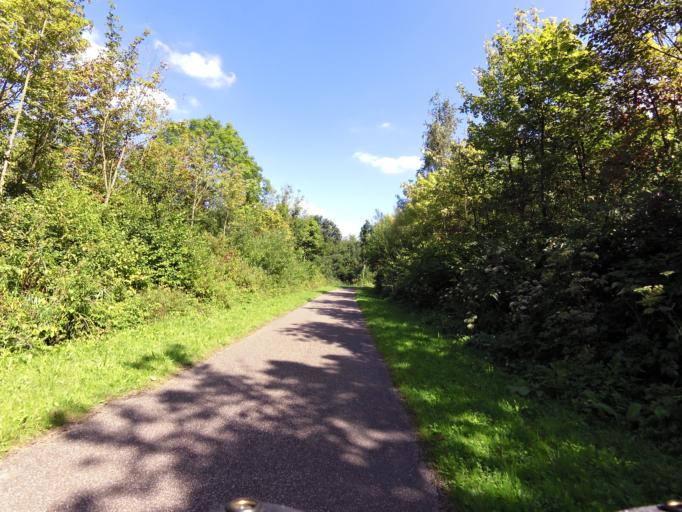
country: NL
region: South Holland
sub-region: Gemeente Barendrecht
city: Barendrecht
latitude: 51.8670
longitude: 4.5219
